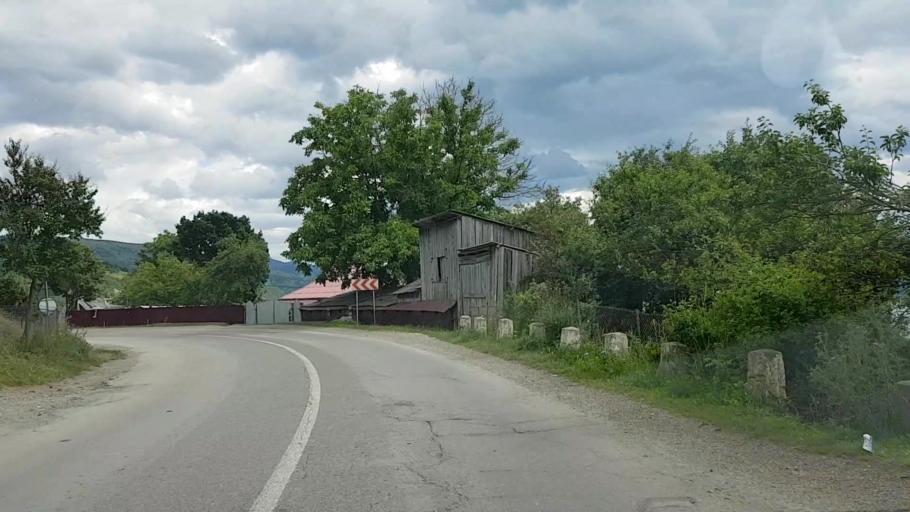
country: RO
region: Neamt
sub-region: Comuna Hangu
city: Hangu
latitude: 47.0523
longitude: 26.0263
